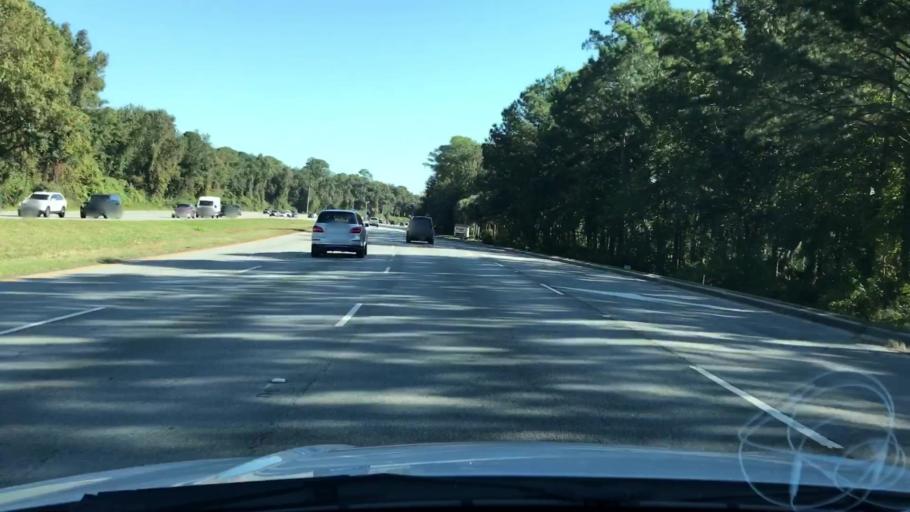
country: US
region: South Carolina
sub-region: Beaufort County
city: Bluffton
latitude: 32.2410
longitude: -80.8205
